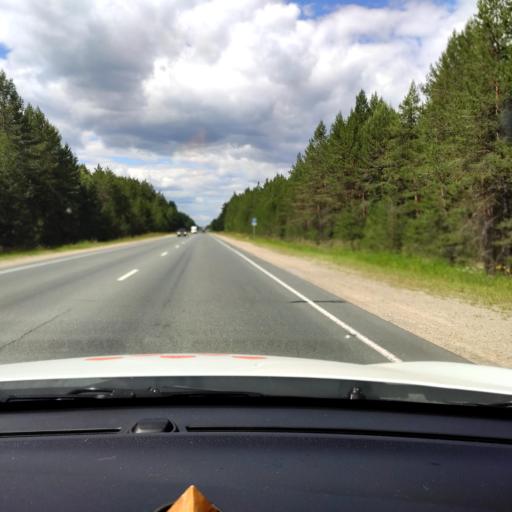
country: RU
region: Mariy-El
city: Krasnogorskiy
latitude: 56.0668
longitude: 48.3661
